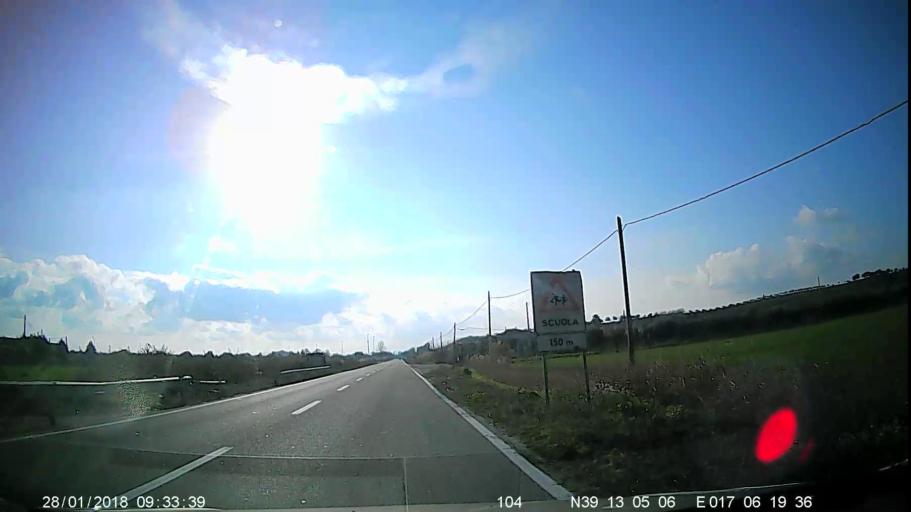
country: IT
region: Calabria
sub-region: Provincia di Crotone
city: Tronca
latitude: 39.2176
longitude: 17.1056
